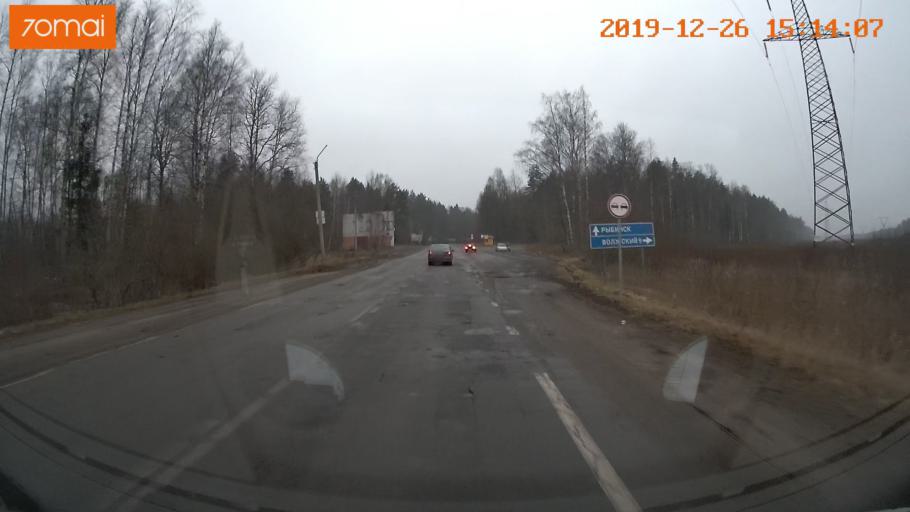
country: RU
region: Jaroslavl
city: Rybinsk
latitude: 58.1088
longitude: 38.8818
